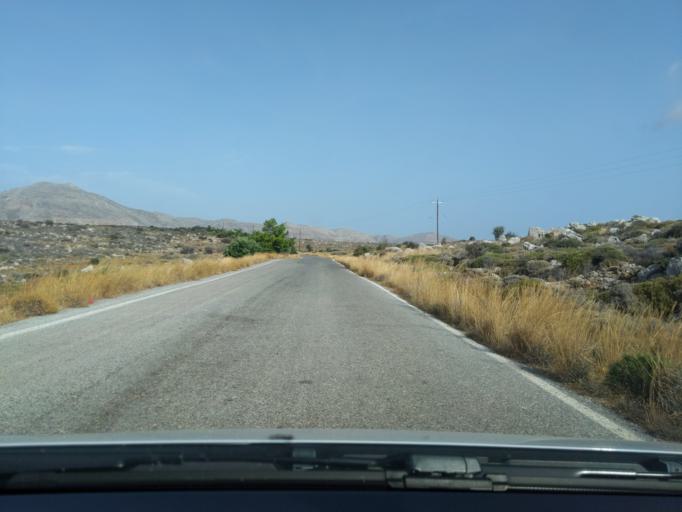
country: GR
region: Crete
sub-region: Nomos Lasithiou
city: Palekastro
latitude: 35.0870
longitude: 26.2429
